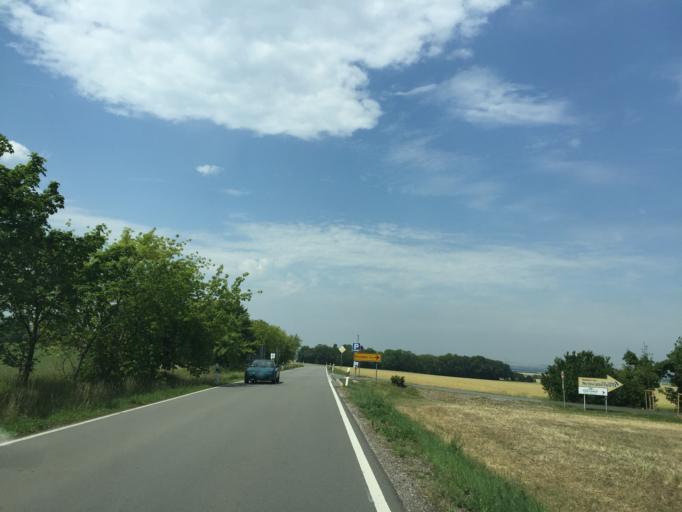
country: DE
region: Thuringia
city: Bosleben-Wullersleben
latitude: 50.8184
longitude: 11.0519
